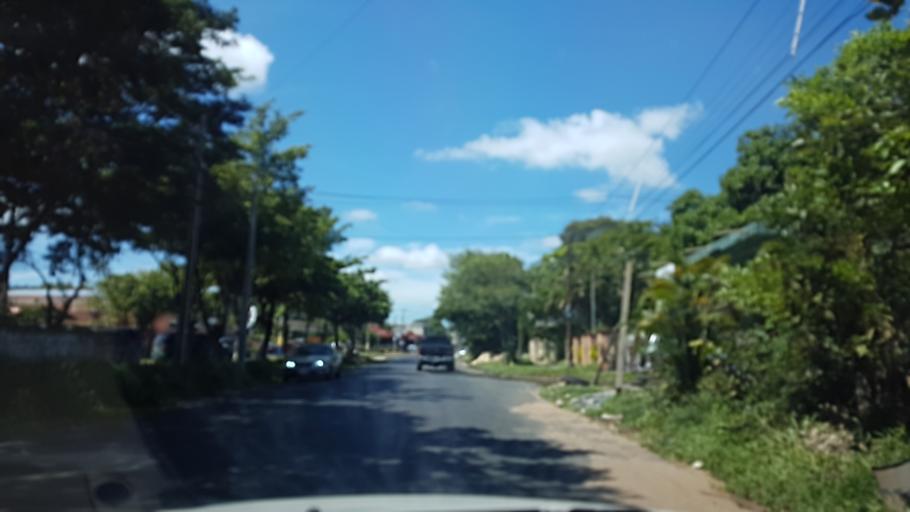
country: PY
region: Central
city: San Lorenzo
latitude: -25.2729
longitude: -57.4963
